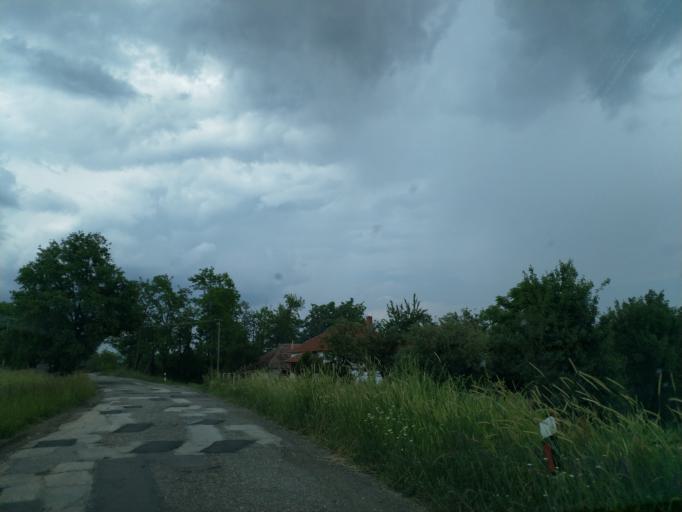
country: RS
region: Central Serbia
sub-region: Zajecarski Okrug
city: Boljevac
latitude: 43.9803
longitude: 21.9728
